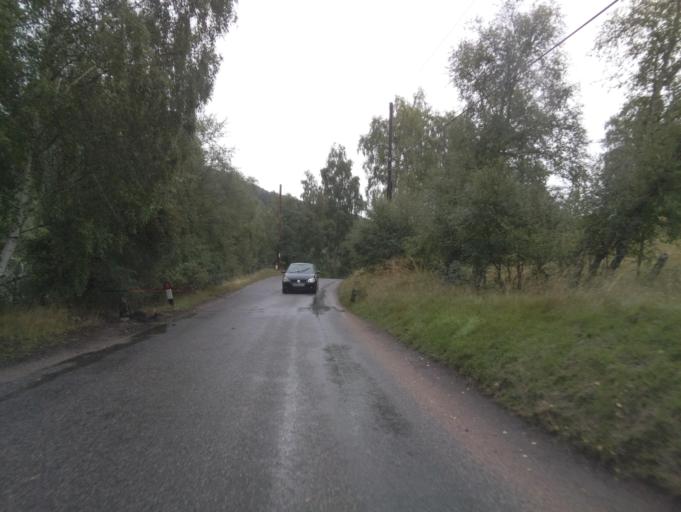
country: GB
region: Scotland
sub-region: Aberdeenshire
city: Ballater
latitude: 57.0793
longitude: -3.0877
